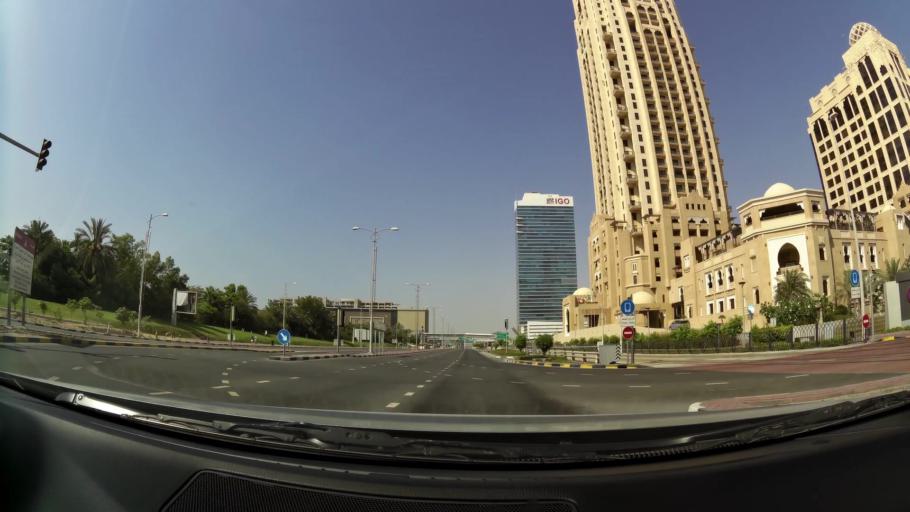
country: AE
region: Dubai
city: Dubai
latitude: 25.0953
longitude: 55.1525
